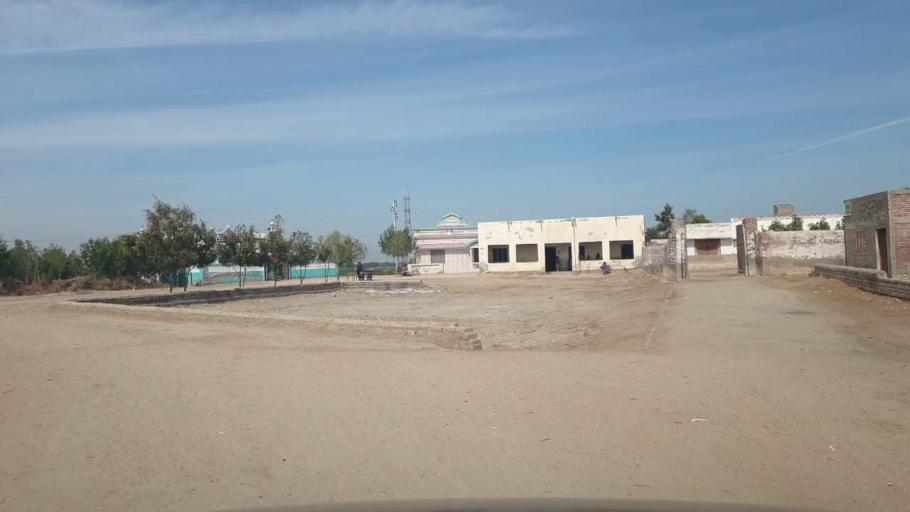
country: PK
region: Sindh
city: Umarkot
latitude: 25.3643
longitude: 69.6100
